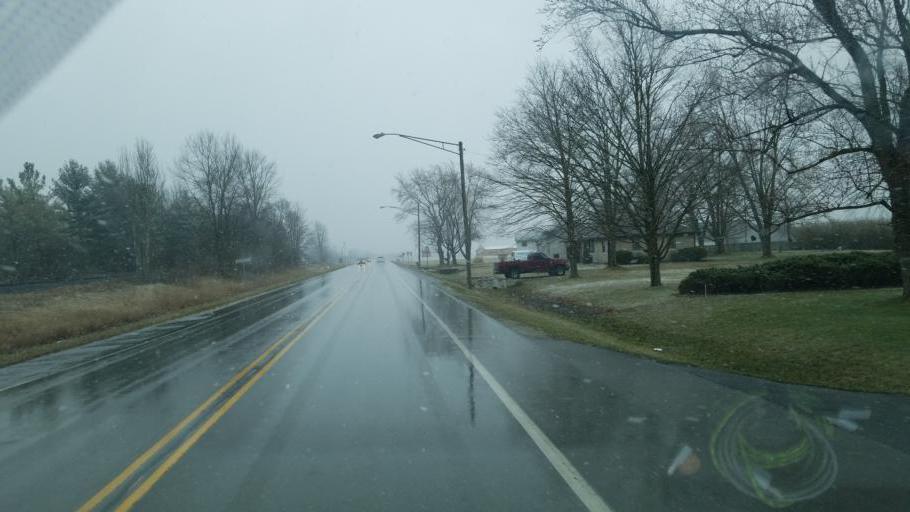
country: US
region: Indiana
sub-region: Wabash County
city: Mount Vernon
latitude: 40.6699
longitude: -85.7227
